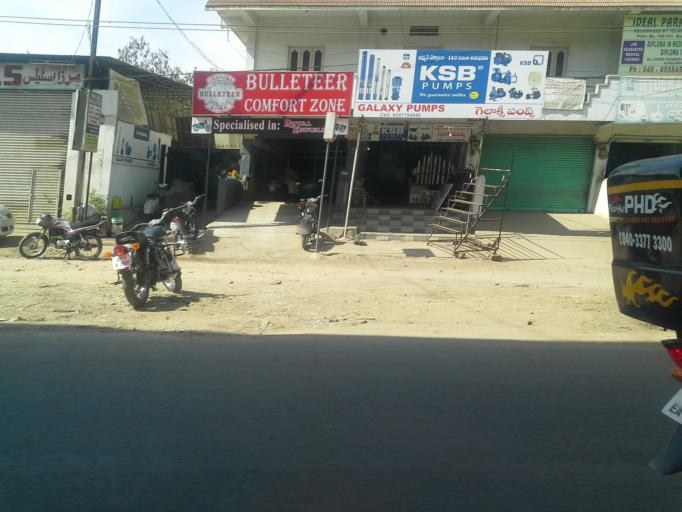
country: IN
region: Telangana
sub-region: Hyderabad
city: Hyderabad
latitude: 17.3753
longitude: 78.4292
